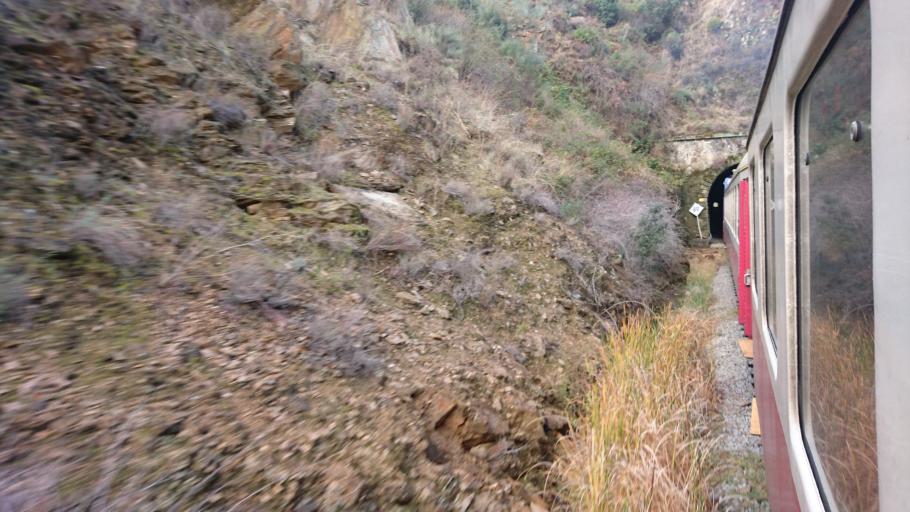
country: PT
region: Guarda
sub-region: Vila Nova de Foz Coa
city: Vila Nova de Foz Coa
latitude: 41.1321
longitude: -7.1421
